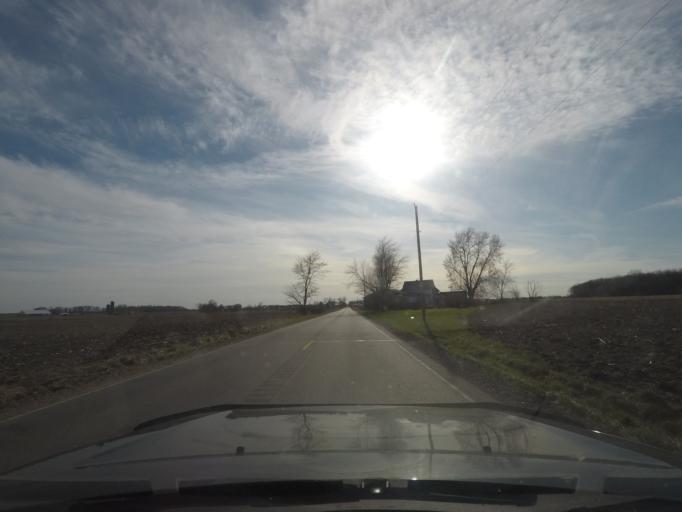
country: US
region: Indiana
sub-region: Elkhart County
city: Wakarusa
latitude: 41.5136
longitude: -85.9853
